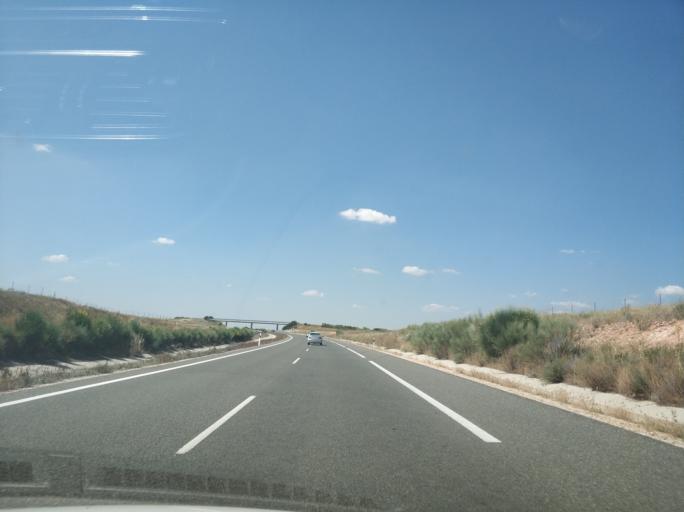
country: ES
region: Castille and Leon
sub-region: Provincia de Salamanca
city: Castellanos de Villiquera
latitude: 41.0473
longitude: -5.6677
